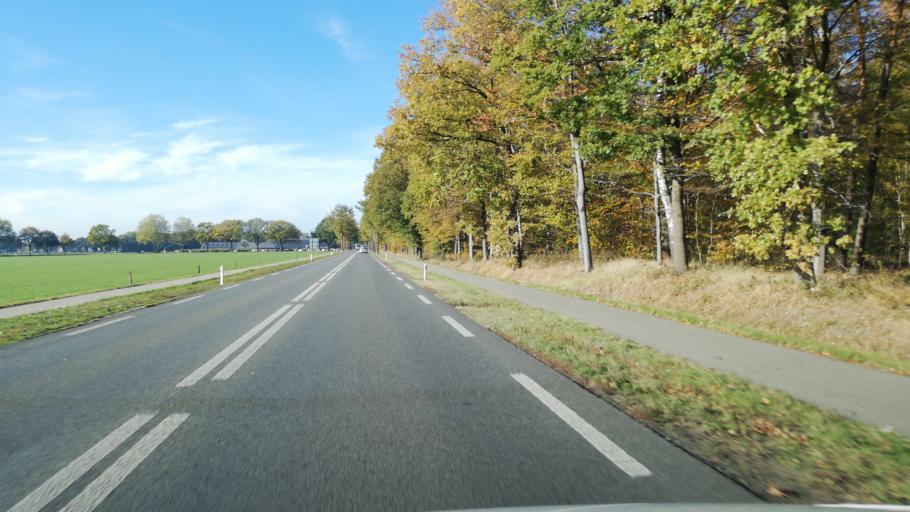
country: NL
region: Gelderland
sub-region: Gemeente Voorst
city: Voorst
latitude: 52.1874
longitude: 6.1002
